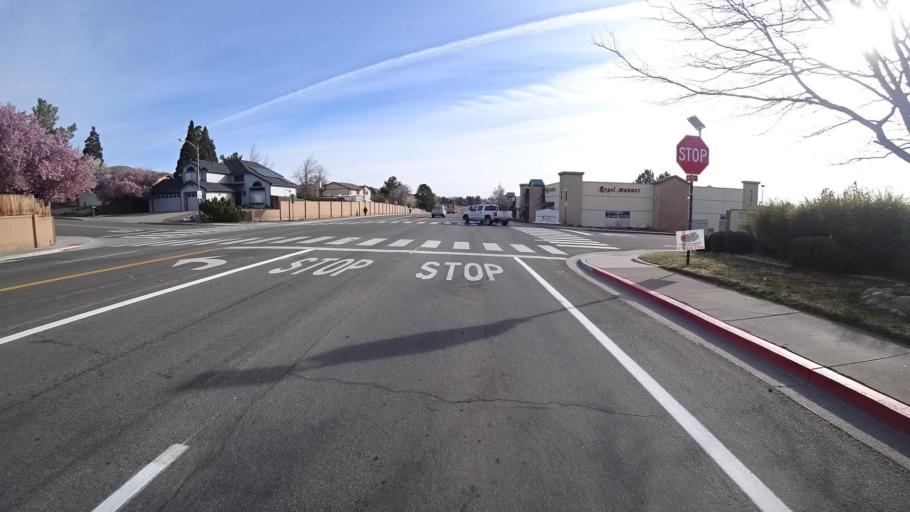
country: US
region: Nevada
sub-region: Washoe County
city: Mogul
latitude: 39.5261
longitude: -119.8884
